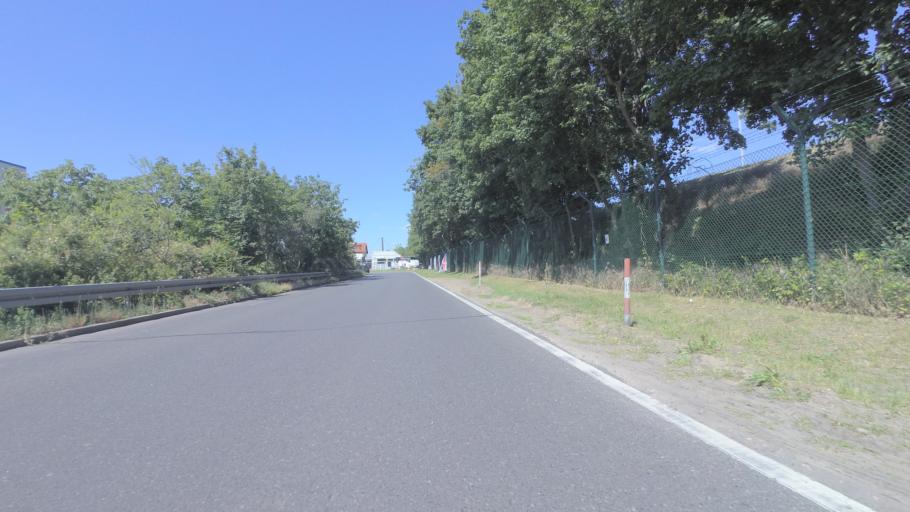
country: DE
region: Brandenburg
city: Rangsdorf
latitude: 52.2957
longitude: 13.4614
